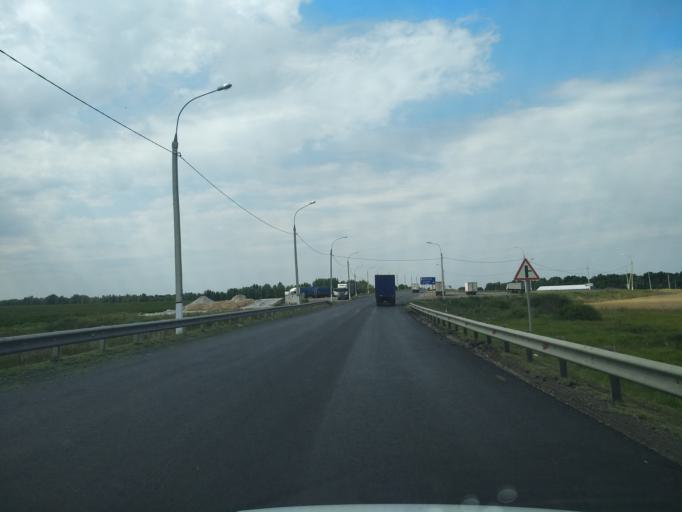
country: RU
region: Voronezj
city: Pereleshino
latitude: 51.7653
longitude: 40.1322
